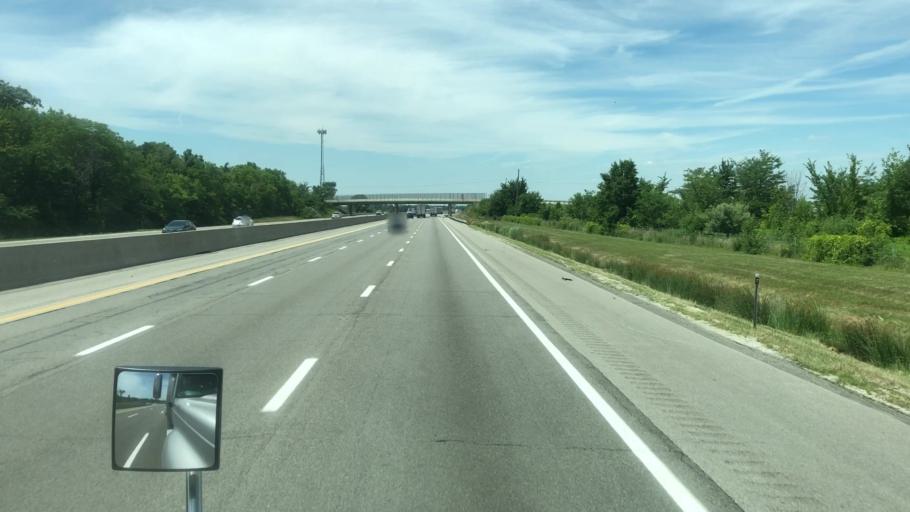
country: US
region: Ohio
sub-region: Ottawa County
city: Elmore
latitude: 41.4710
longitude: -83.3222
